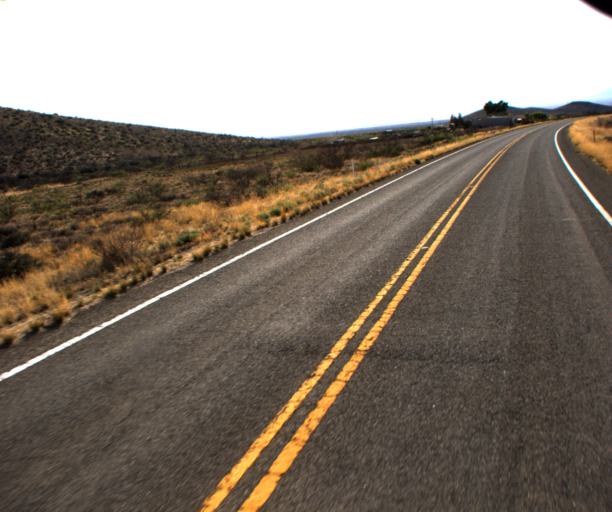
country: US
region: Arizona
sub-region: Cochise County
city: Willcox
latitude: 32.1819
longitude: -109.6604
